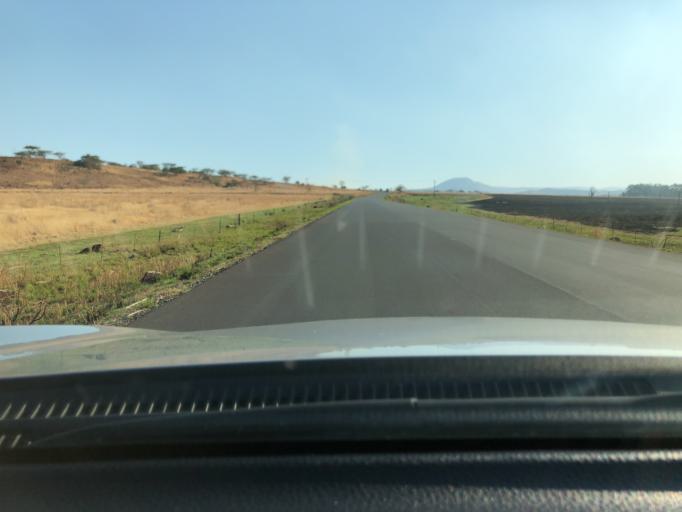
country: ZA
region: KwaZulu-Natal
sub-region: uThukela District Municipality
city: Ekuvukeni
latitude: -28.3612
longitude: 30.0090
